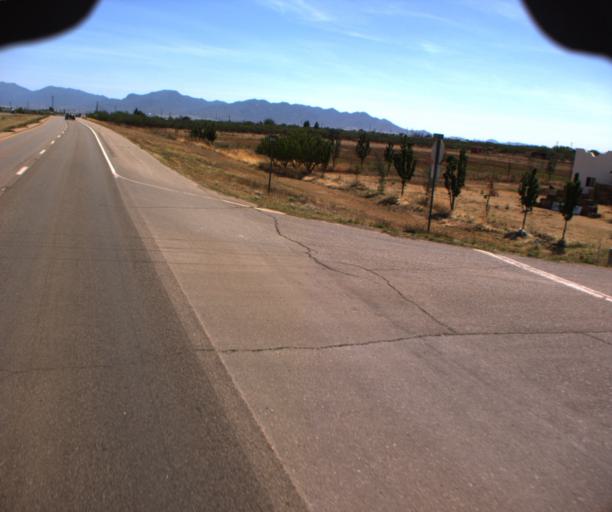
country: US
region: Arizona
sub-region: Cochise County
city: Huachuca City
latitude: 31.7015
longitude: -110.3505
